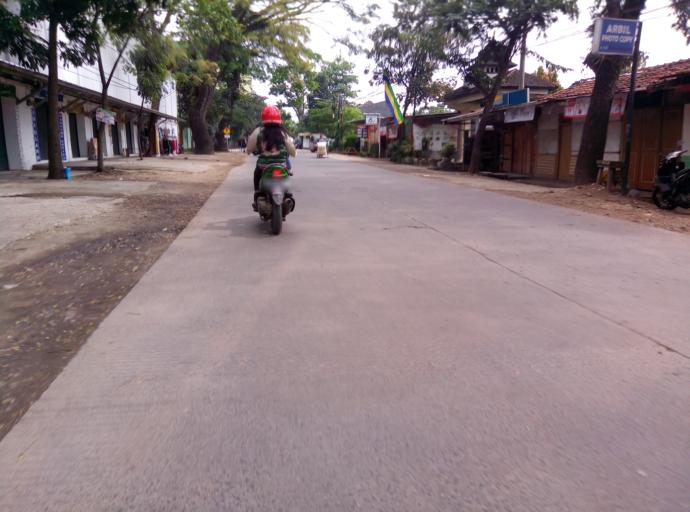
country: ID
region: West Java
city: Bandung
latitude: -6.9300
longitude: 107.6481
